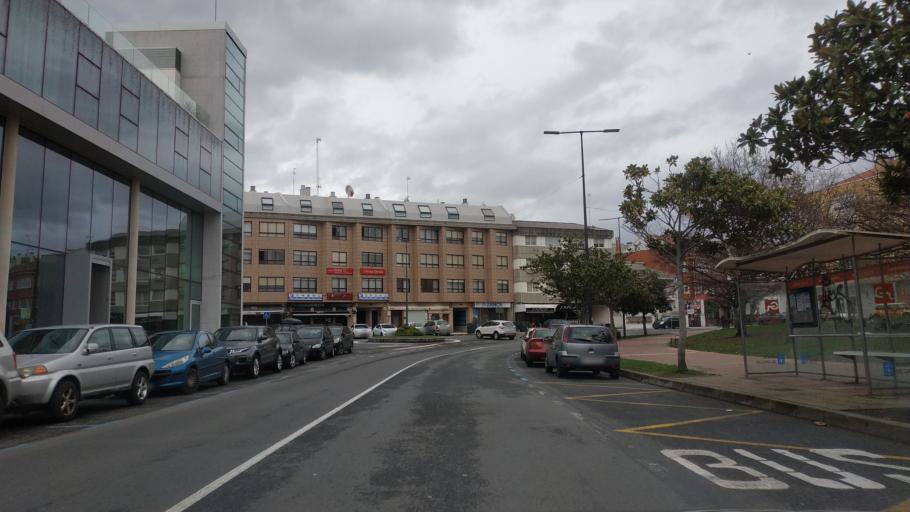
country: ES
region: Galicia
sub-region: Provincia da Coruna
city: Oleiros
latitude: 43.3485
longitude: -8.3461
